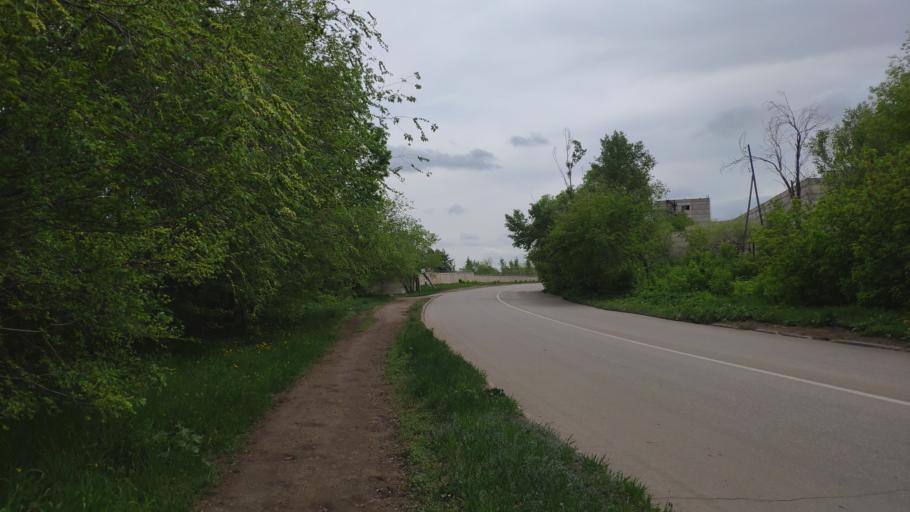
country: RU
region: Chelyabinsk
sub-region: Gorod Magnitogorsk
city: Magnitogorsk
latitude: 53.4157
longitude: 58.9560
